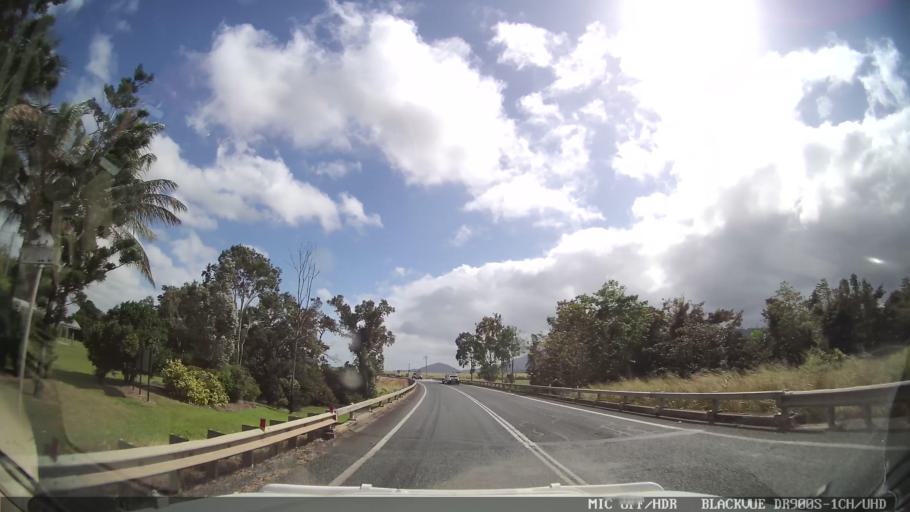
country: AU
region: Queensland
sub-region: Whitsunday
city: Proserpine
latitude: -20.3509
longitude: 148.5561
